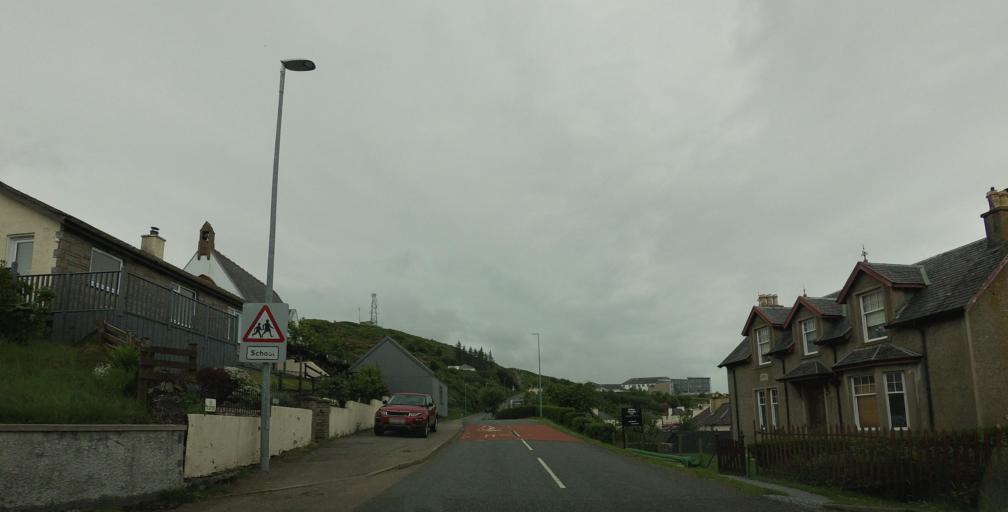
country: GB
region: Scotland
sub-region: Highland
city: Portree
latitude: 57.0038
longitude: -5.8297
